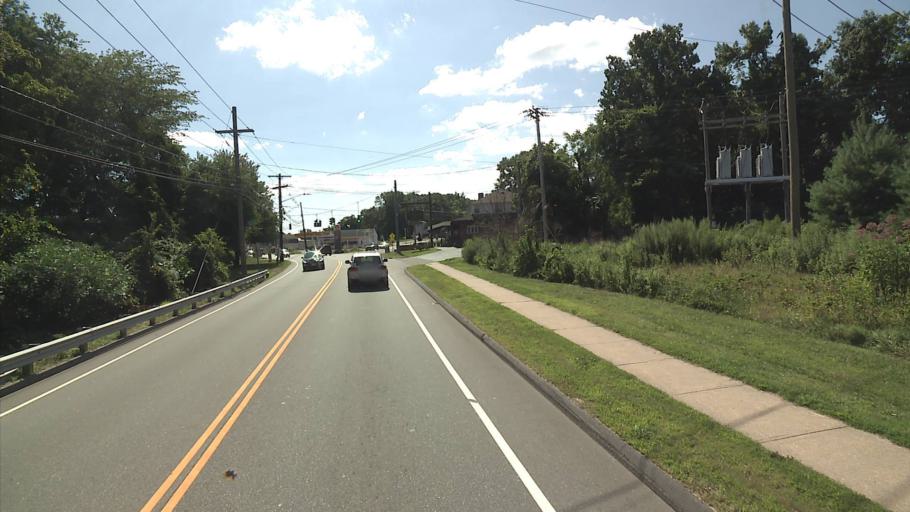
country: US
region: Connecticut
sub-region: Middlesex County
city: Clinton
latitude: 41.2744
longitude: -72.5104
